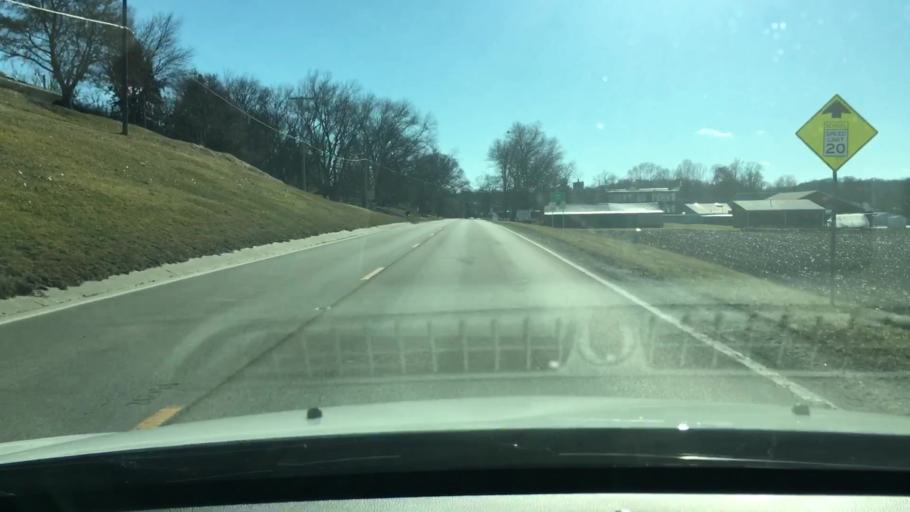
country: US
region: Illinois
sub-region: Morgan County
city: Meredosia
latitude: 39.7567
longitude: -90.5351
